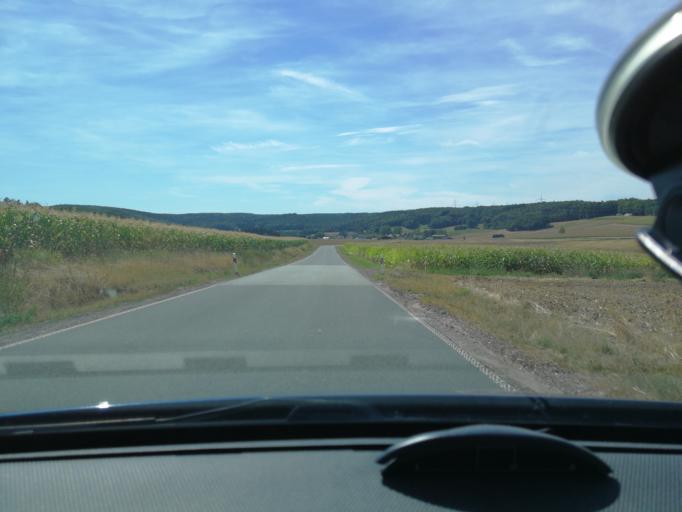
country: DE
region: Rheinland-Pfalz
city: Heidweiler
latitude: 49.9179
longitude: 6.7587
